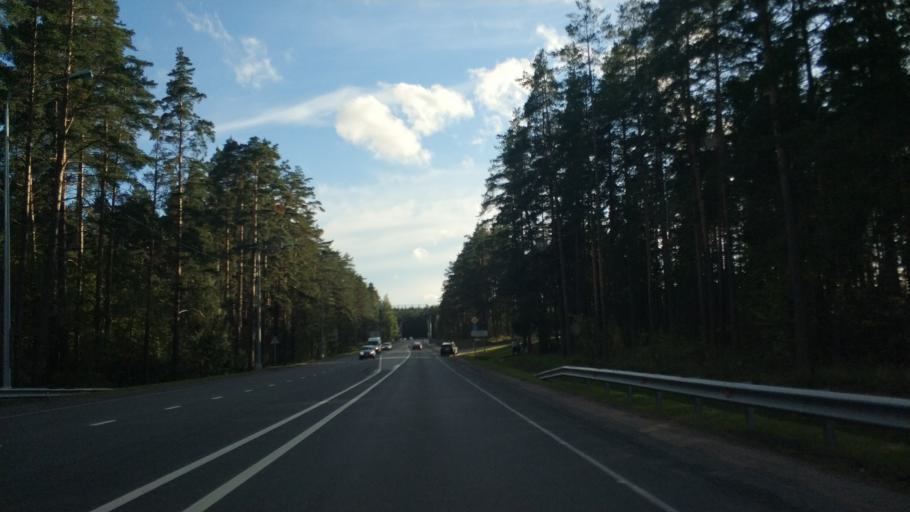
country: RU
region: Leningrad
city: Sapernoye
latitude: 60.7112
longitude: 29.9743
